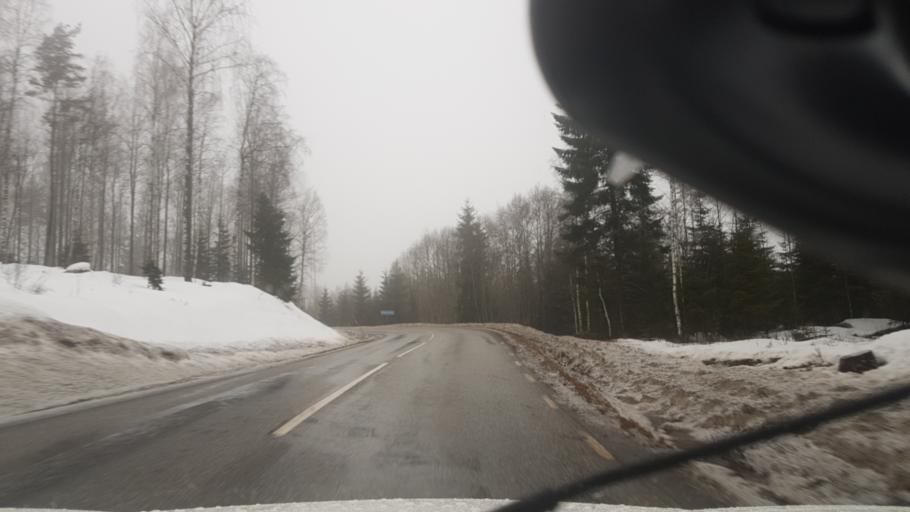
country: SE
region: Vaermland
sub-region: Eda Kommun
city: Amotfors
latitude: 59.5799
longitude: 12.2615
